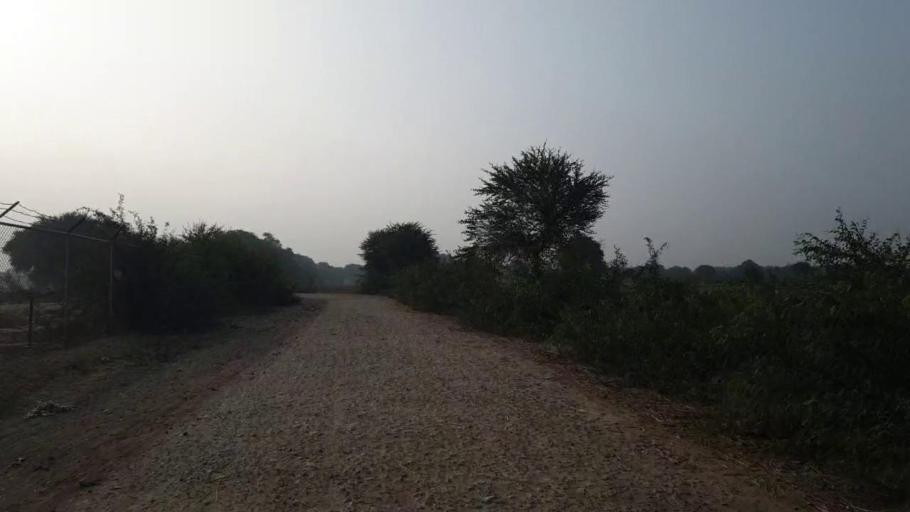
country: PK
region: Sindh
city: Tando Muhammad Khan
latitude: 25.1787
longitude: 68.6021
